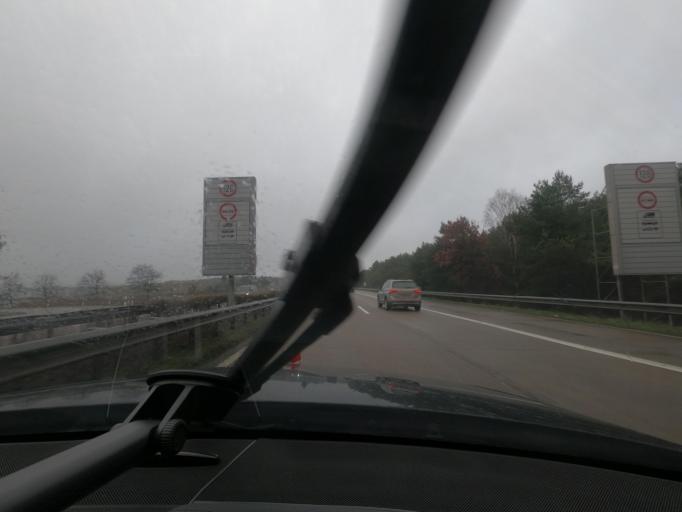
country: DE
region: Lower Saxony
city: Soltau
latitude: 53.0011
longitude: 9.9289
